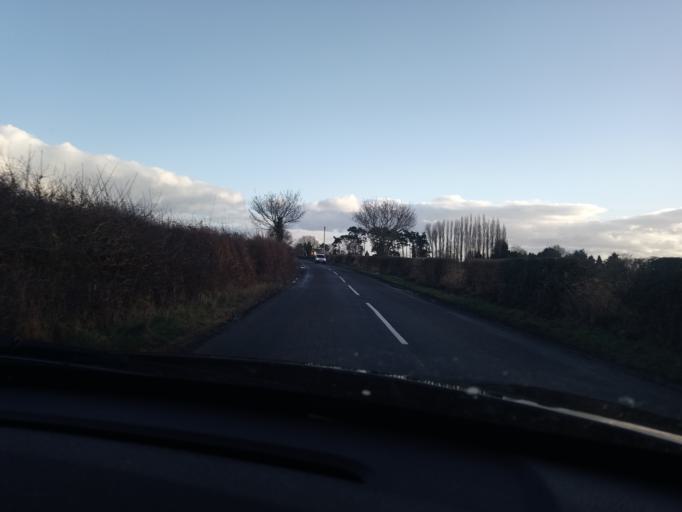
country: GB
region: England
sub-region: Shropshire
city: Petton
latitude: 52.8924
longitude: -2.7943
